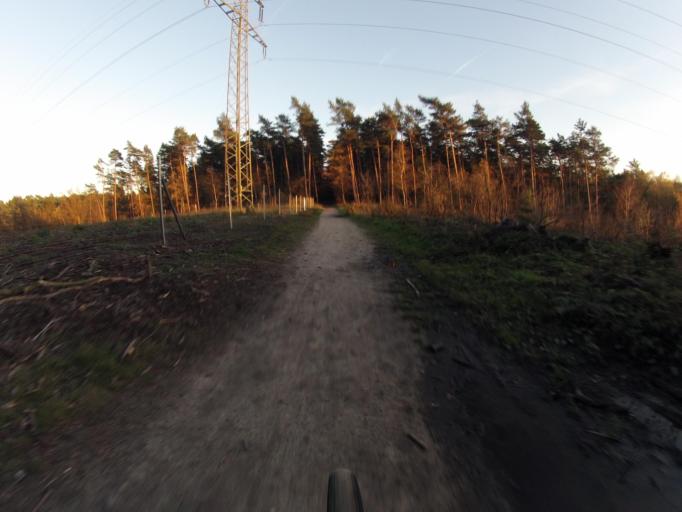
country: DE
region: North Rhine-Westphalia
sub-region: Regierungsbezirk Munster
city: Birgte
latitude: 52.2661
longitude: 7.6506
